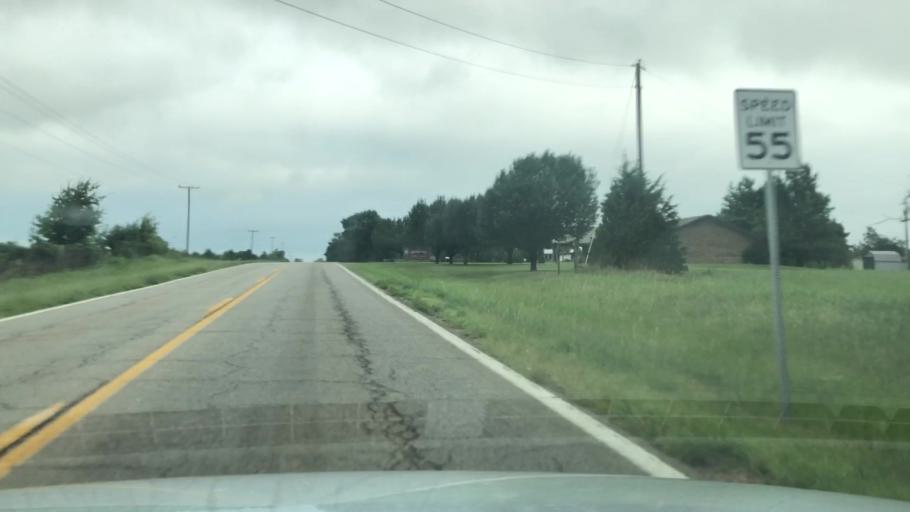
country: US
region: Oklahoma
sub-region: Nowata County
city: Nowata
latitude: 36.7086
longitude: -95.6566
